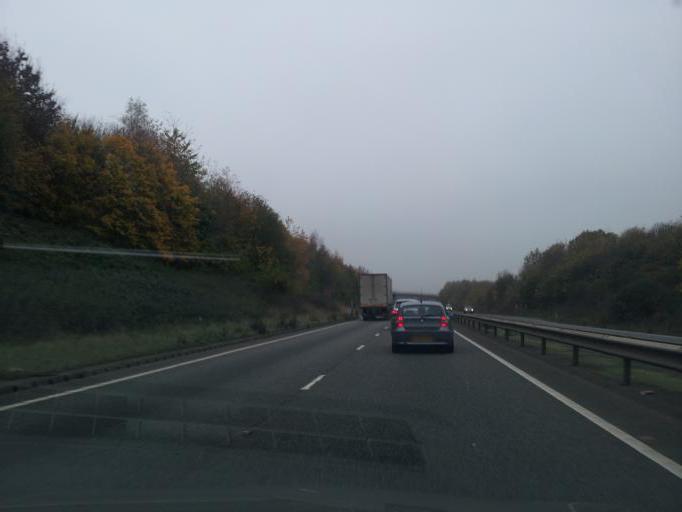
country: GB
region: England
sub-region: Leicestershire
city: Anstey
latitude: 52.6782
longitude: -1.1722
